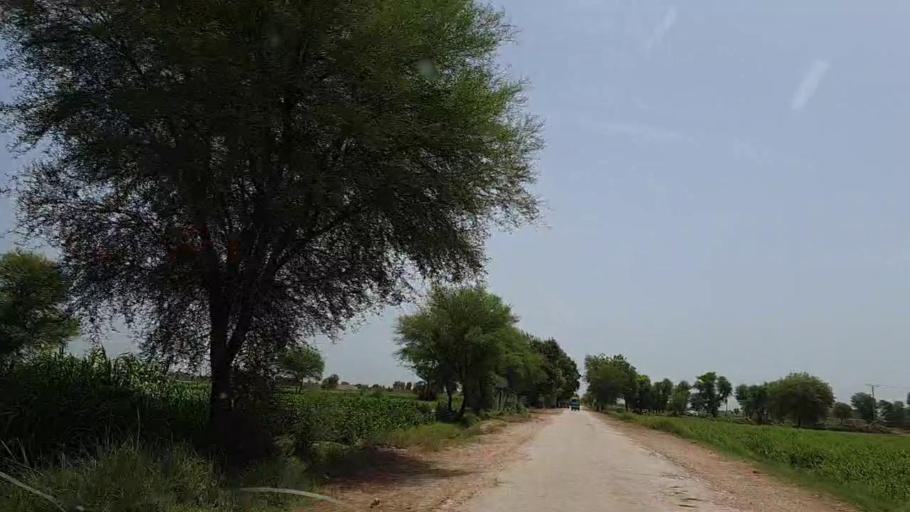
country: PK
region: Sindh
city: Tharu Shah
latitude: 26.9650
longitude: 68.0505
